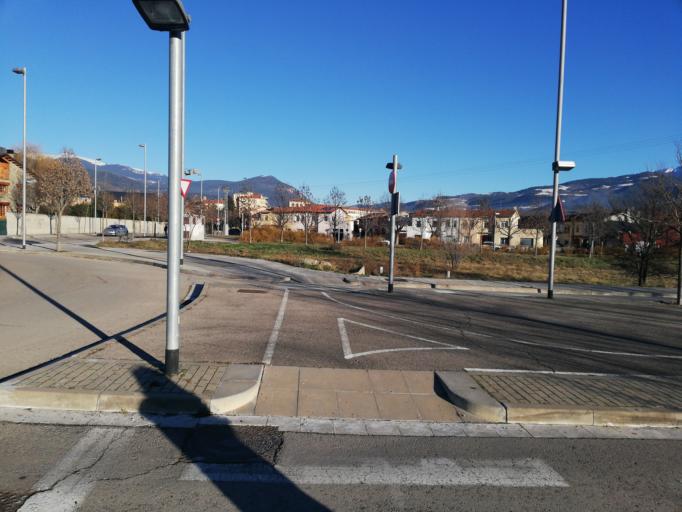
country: ES
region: Catalonia
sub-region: Provincia de Lleida
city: la Seu d'Urgell
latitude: 42.3525
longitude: 1.4519
